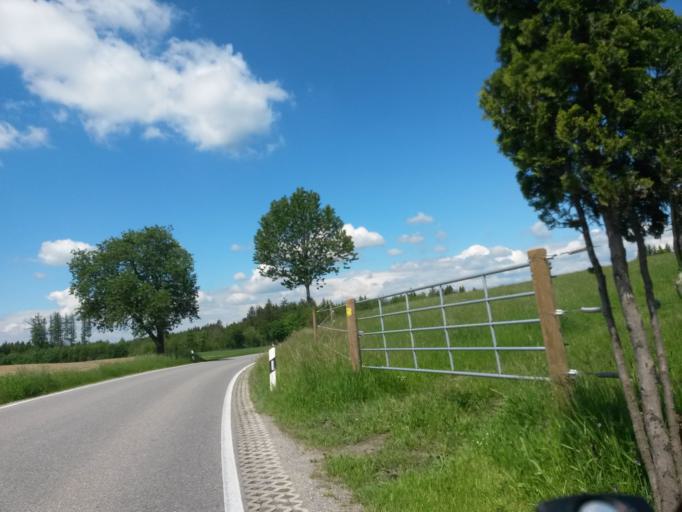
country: DE
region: Baden-Wuerttemberg
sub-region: Tuebingen Region
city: Bad Waldsee
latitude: 47.9365
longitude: 9.7190
